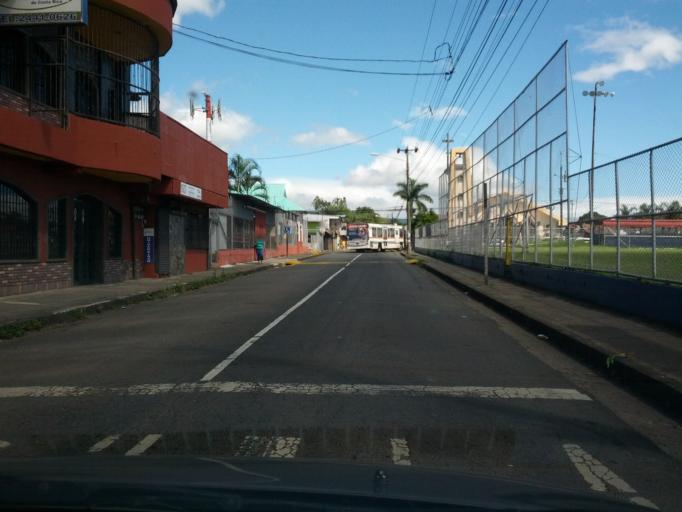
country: CR
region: Alajuela
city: Alajuela
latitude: 10.0203
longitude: -84.2080
